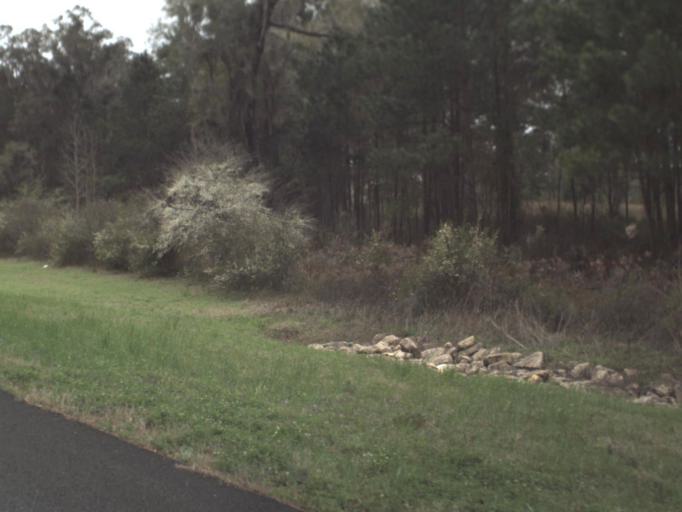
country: US
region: Florida
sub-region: Leon County
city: Tallahassee
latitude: 30.6176
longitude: -84.1720
